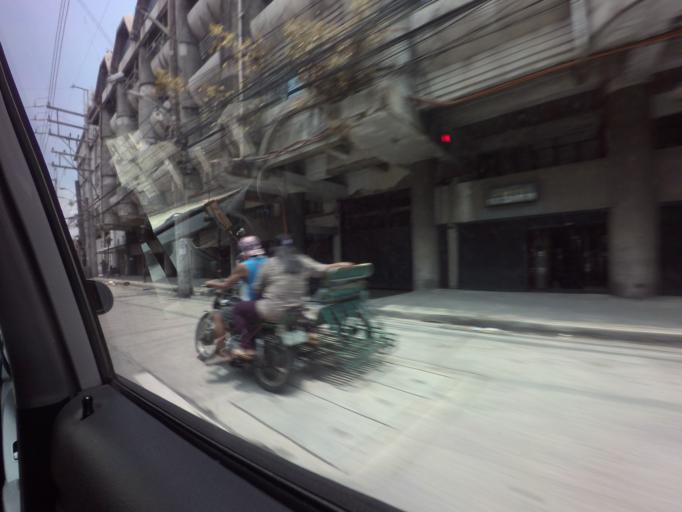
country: PH
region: Metro Manila
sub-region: City of Manila
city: Quiapo
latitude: 14.5944
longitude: 120.9847
